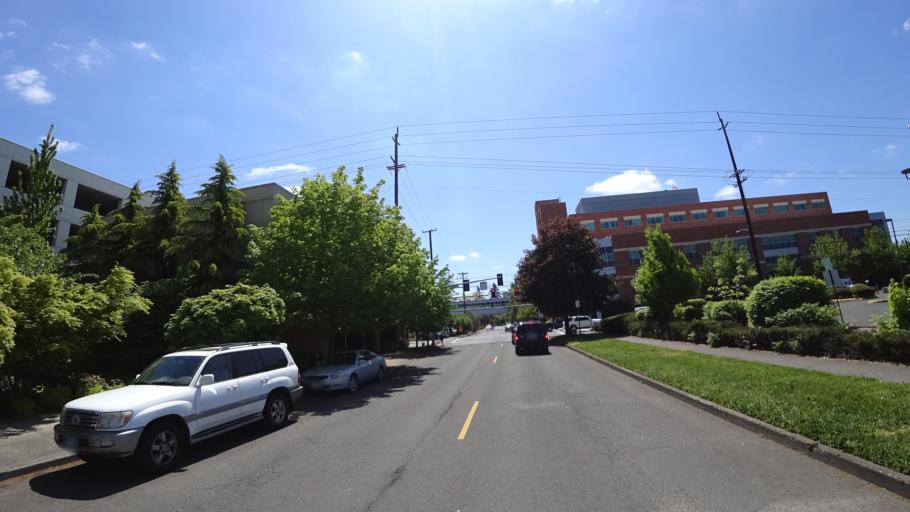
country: US
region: Oregon
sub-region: Washington County
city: Hillsboro
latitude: 45.5205
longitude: -122.9790
